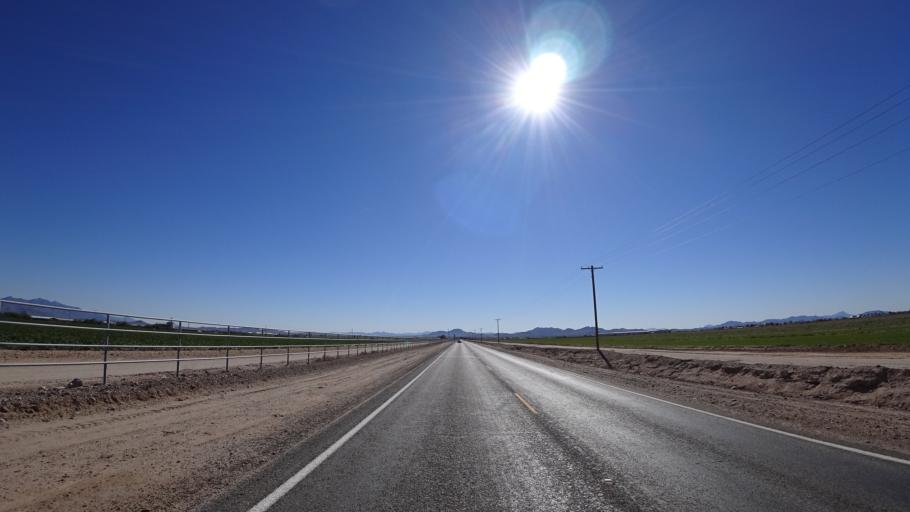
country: US
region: Arizona
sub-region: Maricopa County
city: Buckeye
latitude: 33.4026
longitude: -112.5215
